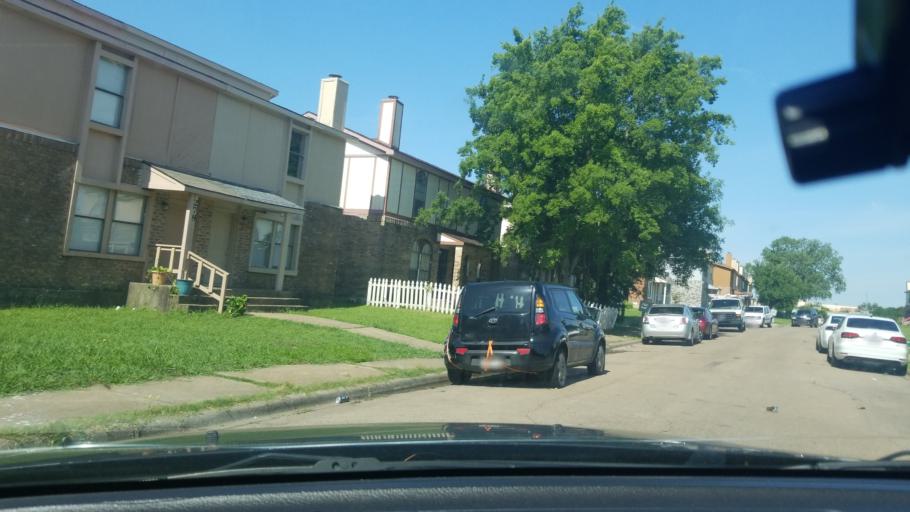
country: US
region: Texas
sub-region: Dallas County
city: Mesquite
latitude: 32.7783
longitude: -96.5940
